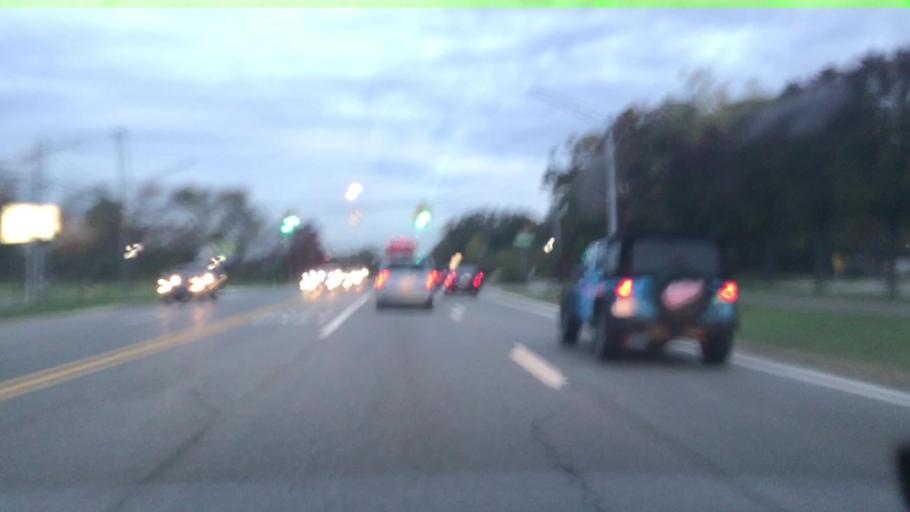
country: US
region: Michigan
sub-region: Oakland County
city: Bloomfield Hills
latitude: 42.6256
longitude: -83.2490
